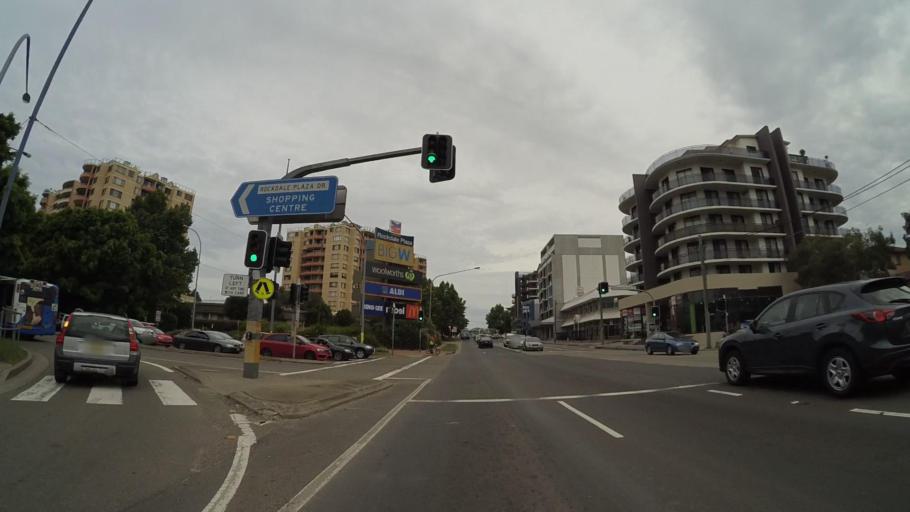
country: AU
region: New South Wales
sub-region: Rockdale
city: Banksia
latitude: -33.9569
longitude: 151.1379
